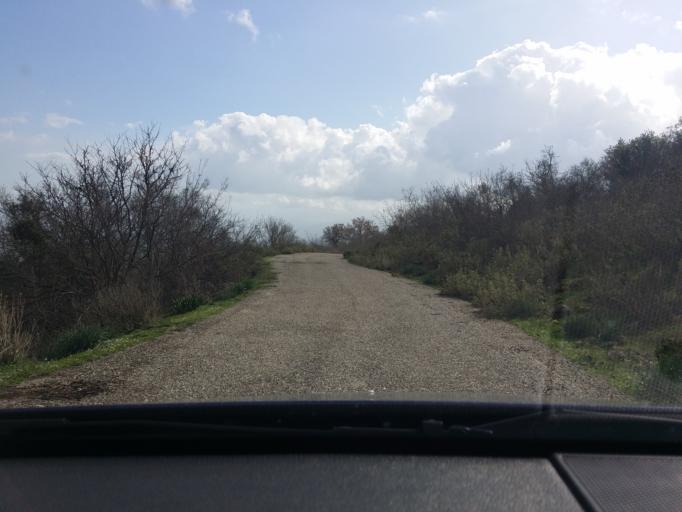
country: GR
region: West Greece
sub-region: Nomos Aitolias kai Akarnanias
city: Fitiai
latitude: 38.6377
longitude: 21.1967
